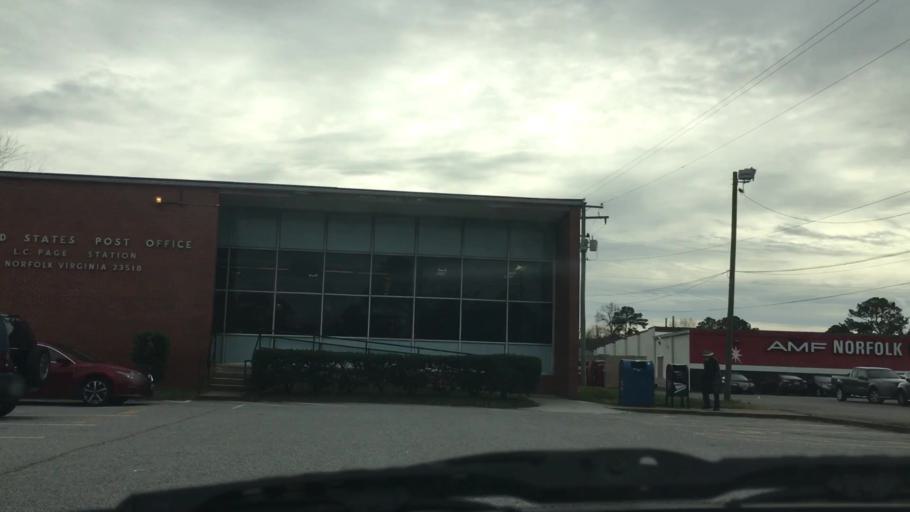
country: US
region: Virginia
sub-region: City of Norfolk
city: Norfolk
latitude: 36.9149
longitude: -76.2136
